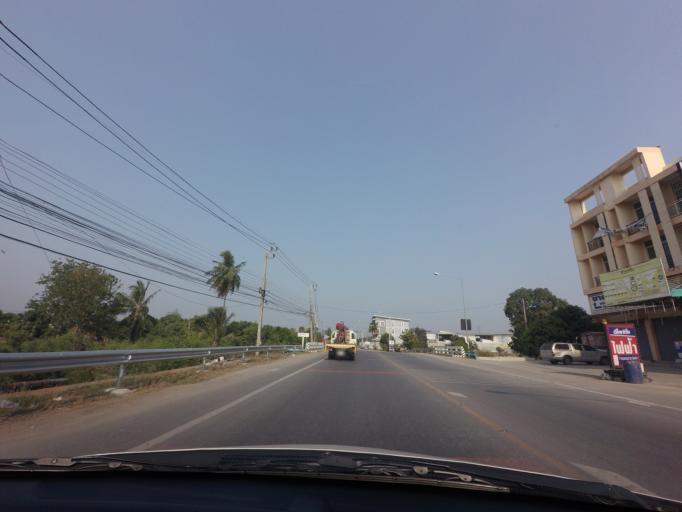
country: TH
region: Bangkok
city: Thawi Watthana
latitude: 13.8115
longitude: 100.3497
